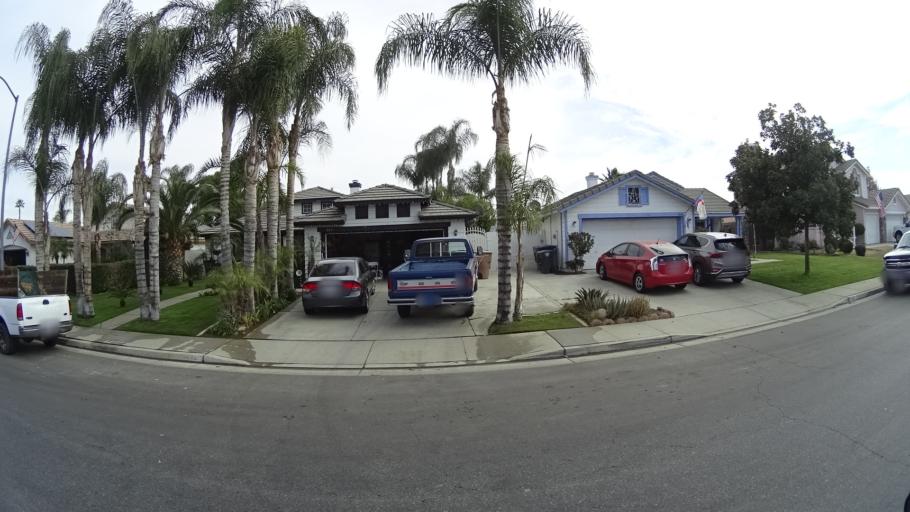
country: US
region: California
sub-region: Kern County
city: Rosedale
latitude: 35.3993
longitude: -119.1323
